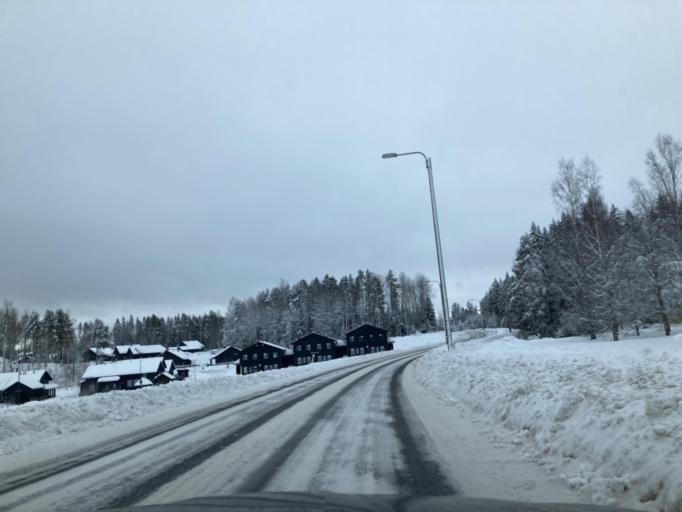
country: FI
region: Central Finland
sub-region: Jaemsae
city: Jaemsae
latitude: 61.8774
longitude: 25.2793
